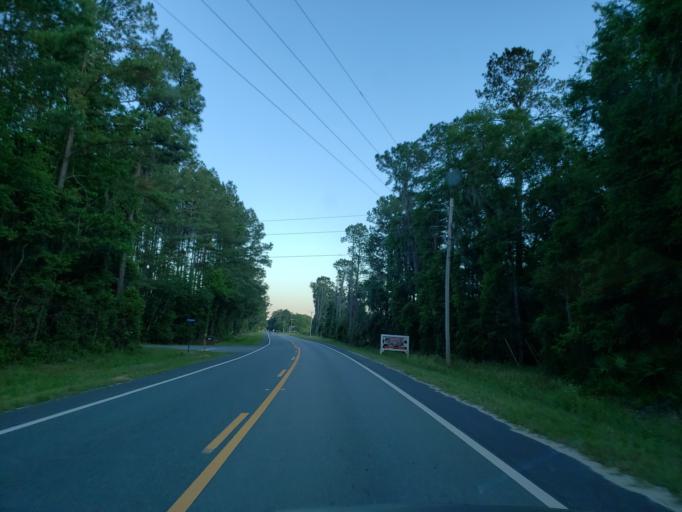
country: US
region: Georgia
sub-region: Echols County
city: Statenville
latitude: 30.5747
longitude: -83.1655
